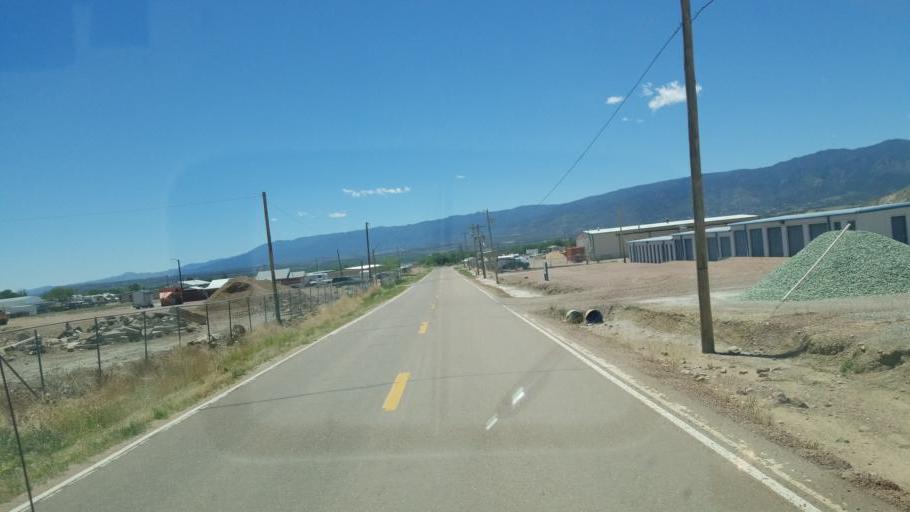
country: US
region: Colorado
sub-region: Fremont County
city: Canon City
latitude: 38.4750
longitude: -105.2226
